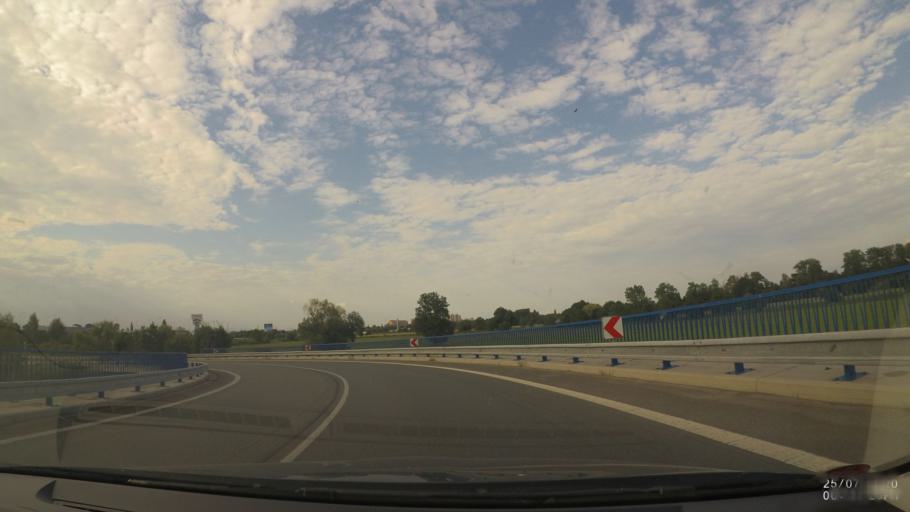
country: CZ
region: Kralovehradecky
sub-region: Okres Hradec Kralove
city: Hradec Kralove
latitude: 50.1859
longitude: 15.8067
